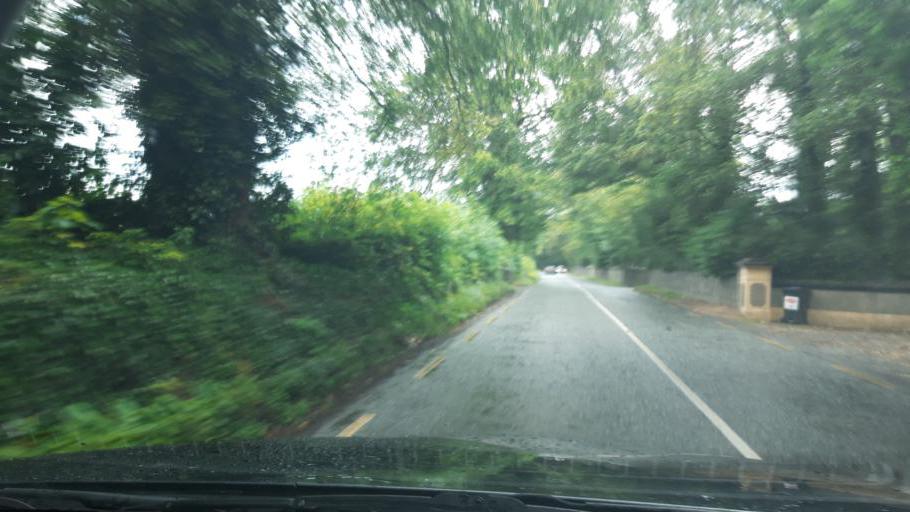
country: IE
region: Leinster
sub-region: An Mhi
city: Dunboyne
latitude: 53.4059
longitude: -6.4457
